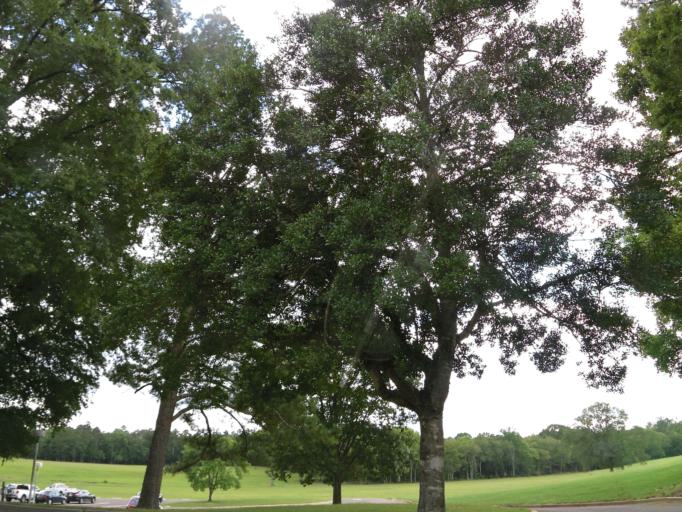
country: US
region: Georgia
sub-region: Catoosa County
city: Fort Oglethorpe
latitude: 34.9401
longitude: -85.2601
